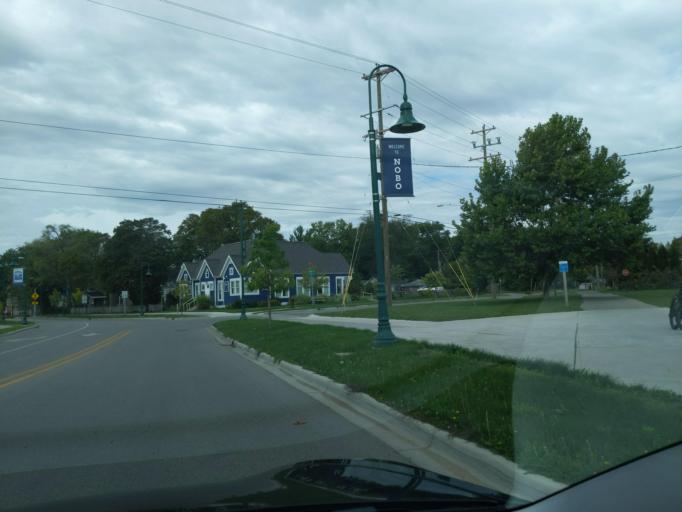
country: US
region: Michigan
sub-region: Grand Traverse County
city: Traverse City
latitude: 44.7593
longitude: -85.6080
